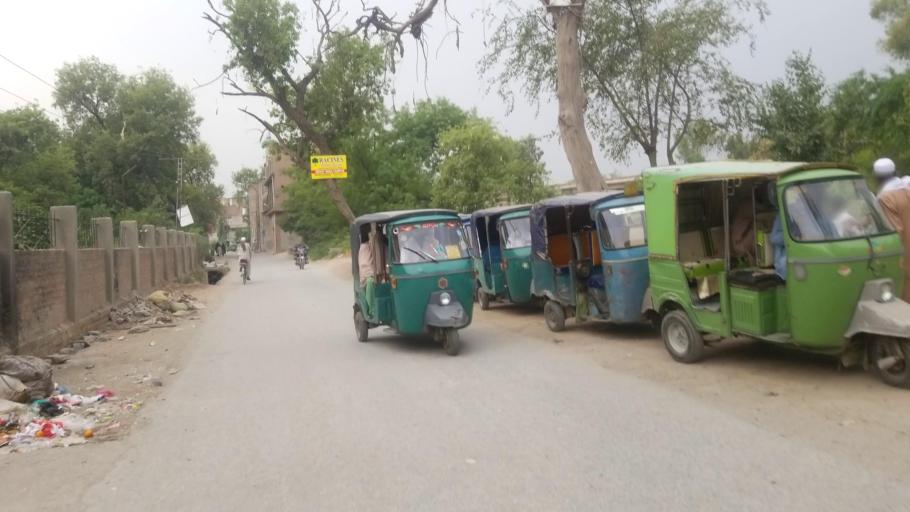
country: PK
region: Khyber Pakhtunkhwa
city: Peshawar
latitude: 33.9961
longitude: 71.5631
